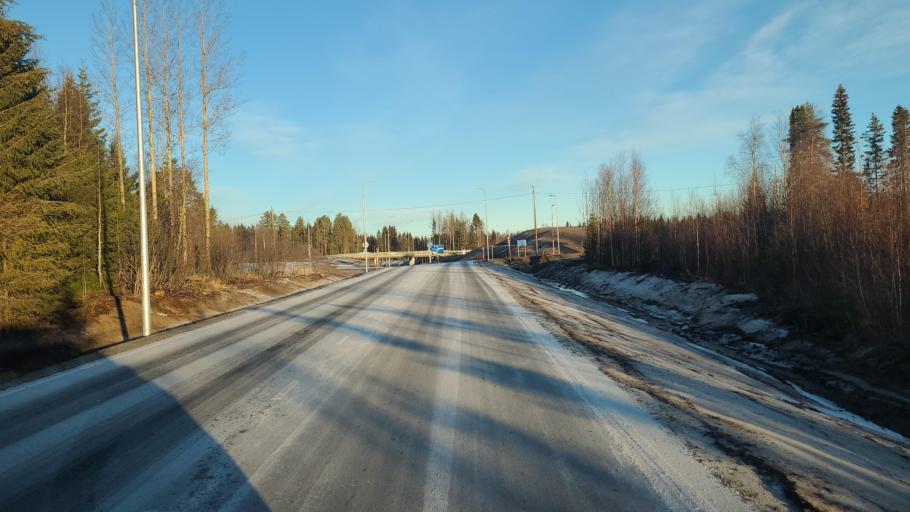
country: FI
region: Lapland
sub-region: Kemi-Tornio
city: Kemi
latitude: 65.6764
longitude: 24.7437
